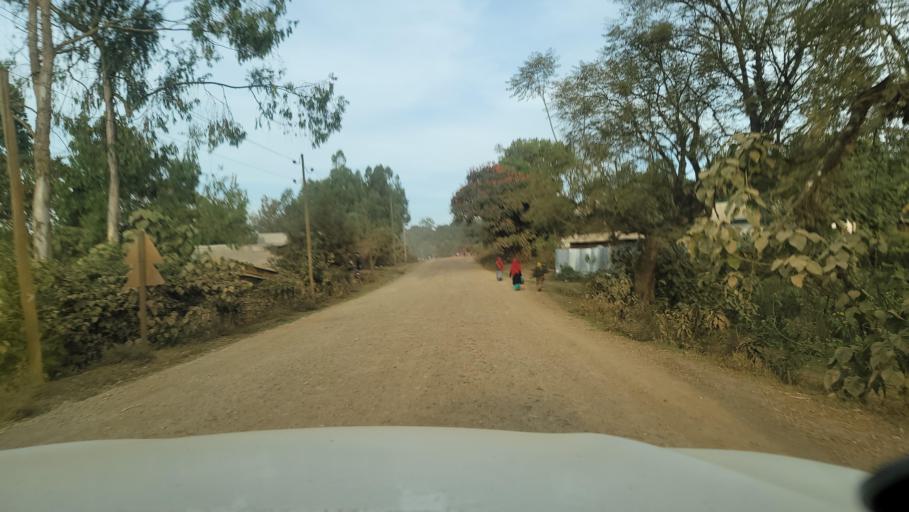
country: ET
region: Oromiya
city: Agaro
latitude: 7.8388
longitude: 36.5565
